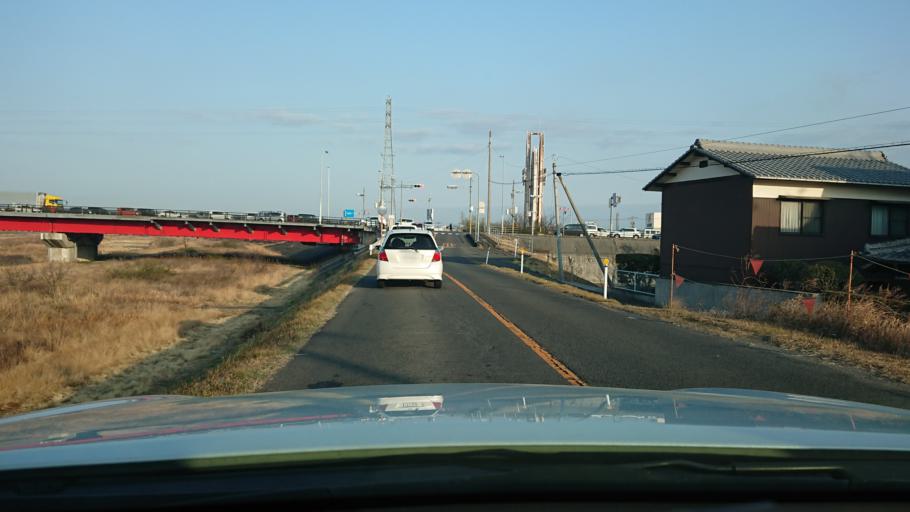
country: JP
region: Kagawa
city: Marugame
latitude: 34.2812
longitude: 133.8213
